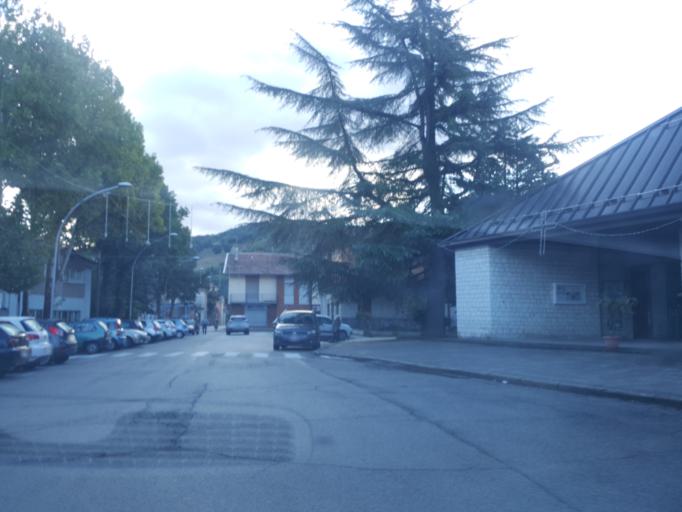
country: IT
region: The Marches
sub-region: Provincia di Macerata
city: Castelraimondo
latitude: 43.2070
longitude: 13.0546
